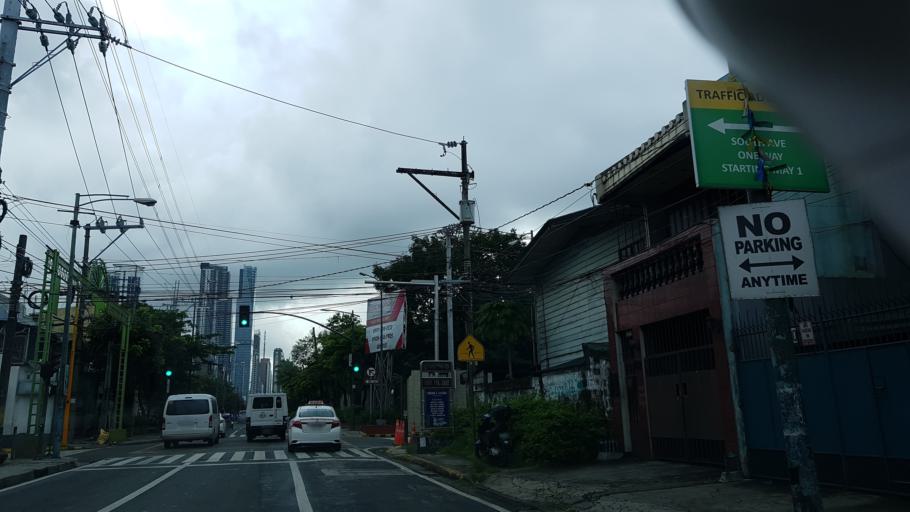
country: PH
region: Metro Manila
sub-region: Makati City
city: Makati City
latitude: 14.5688
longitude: 121.0176
